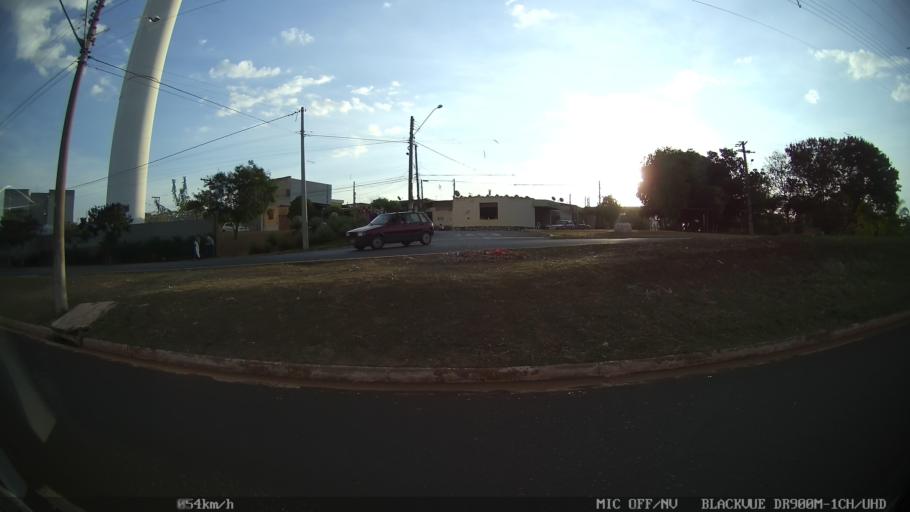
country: BR
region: Sao Paulo
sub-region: Ribeirao Preto
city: Ribeirao Preto
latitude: -21.1318
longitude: -47.8041
